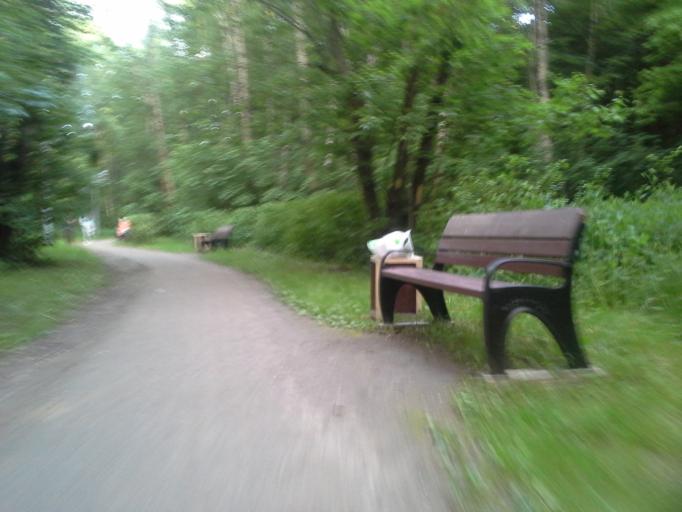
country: RU
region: Moscow
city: Nikulino
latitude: 55.6528
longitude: 37.4616
